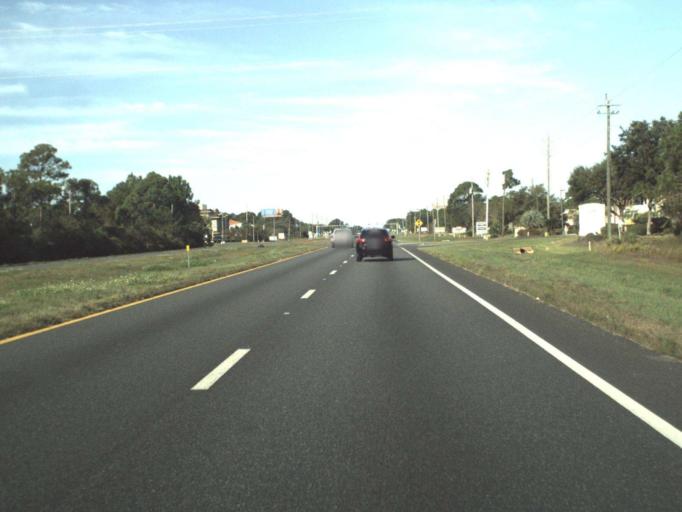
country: US
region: Florida
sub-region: Walton County
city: Miramar Beach
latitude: 30.3851
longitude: -86.3743
